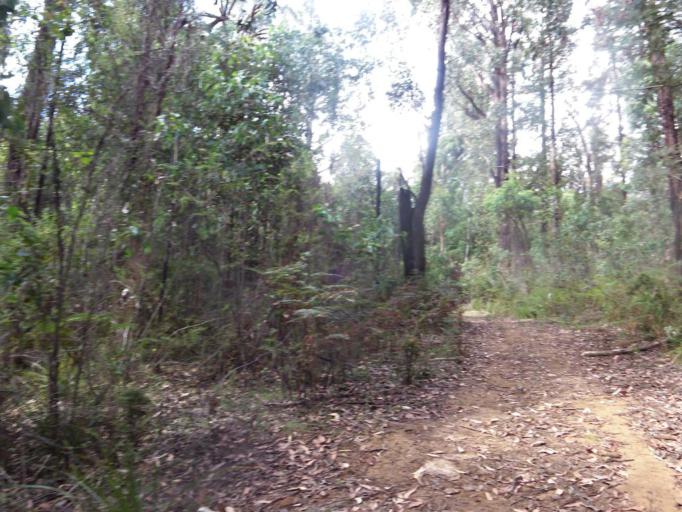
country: AU
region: Victoria
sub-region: Murrindindi
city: Alexandra
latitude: -37.3990
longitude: 145.5790
